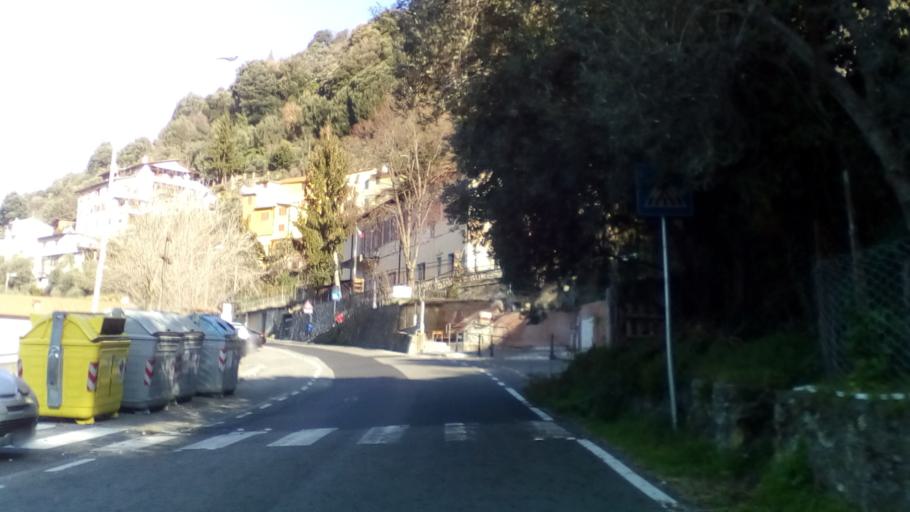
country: IT
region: Tuscany
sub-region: Provincia di Massa-Carrara
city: Montignoso
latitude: 44.0585
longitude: 10.1811
